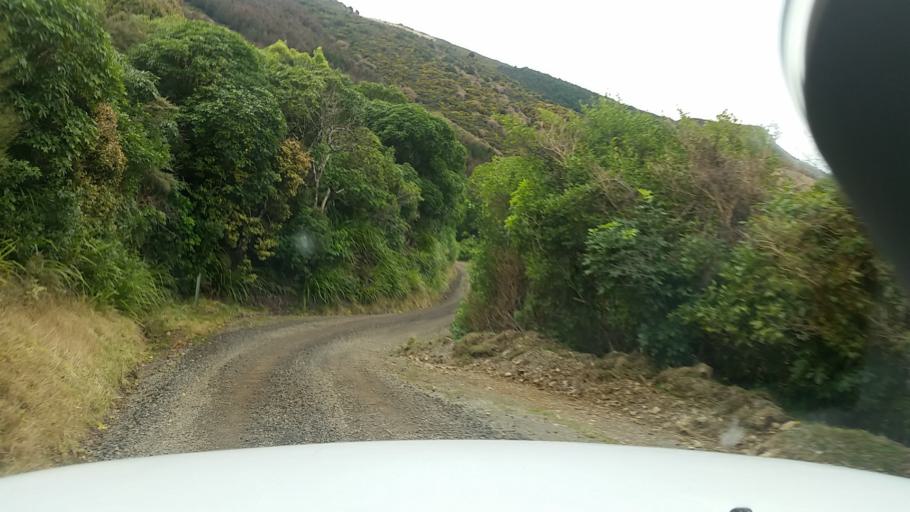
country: NZ
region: Canterbury
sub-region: Christchurch City
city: Christchurch
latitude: -43.7182
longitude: 172.7921
